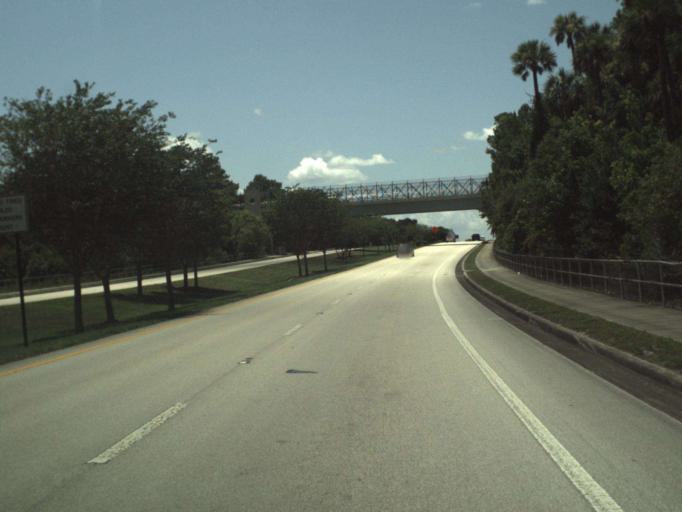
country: US
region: Florida
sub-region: Seminole County
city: Winter Springs
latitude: 28.6921
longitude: -81.2578
